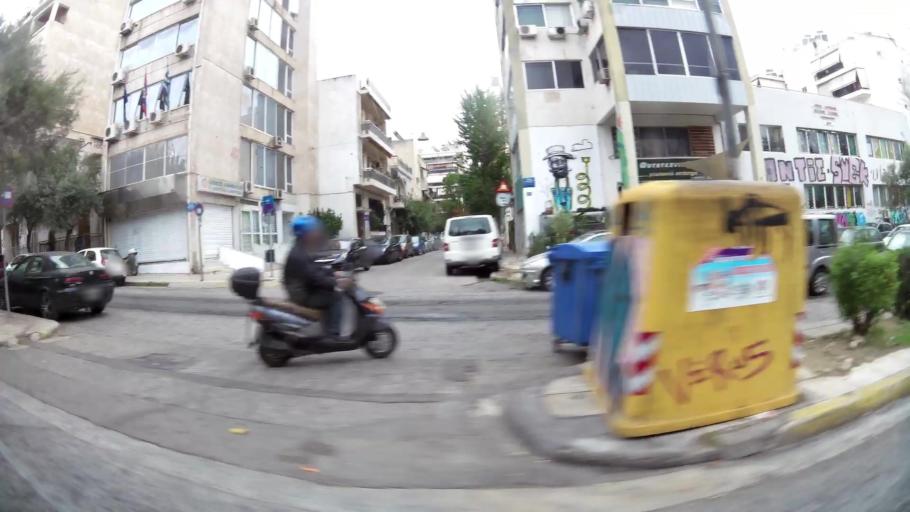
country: GR
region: Attica
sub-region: Nomarchia Athinas
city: Ymittos
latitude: 37.9619
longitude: 23.7400
